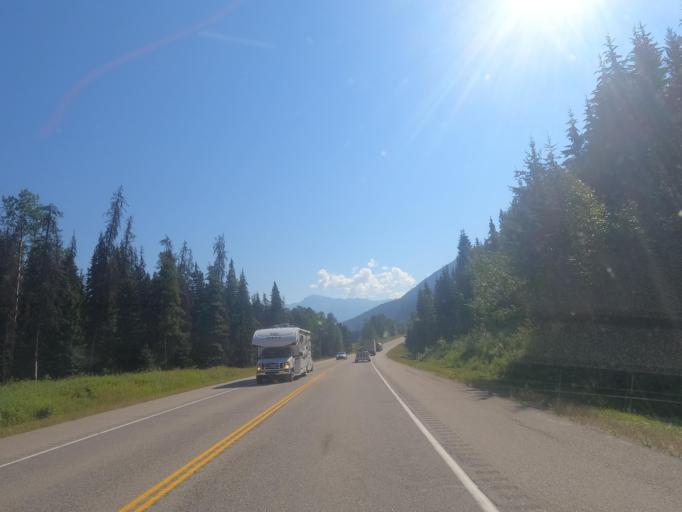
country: CA
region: Alberta
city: Jasper Park Lodge
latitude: 52.8602
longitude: -118.1773
